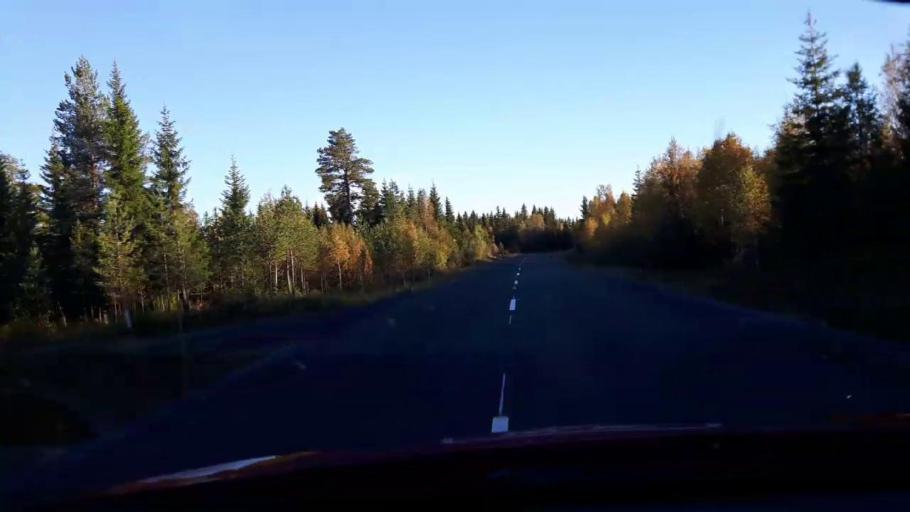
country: SE
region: Jaemtland
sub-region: OEstersunds Kommun
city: Lit
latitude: 63.4892
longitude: 14.8787
